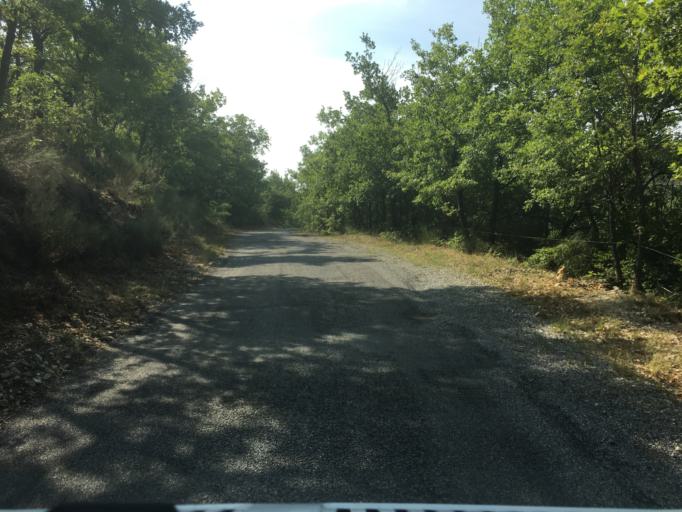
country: FR
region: Provence-Alpes-Cote d'Azur
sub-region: Departement des Alpes-de-Haute-Provence
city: Mallemoisson
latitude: 43.9225
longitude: 6.1912
